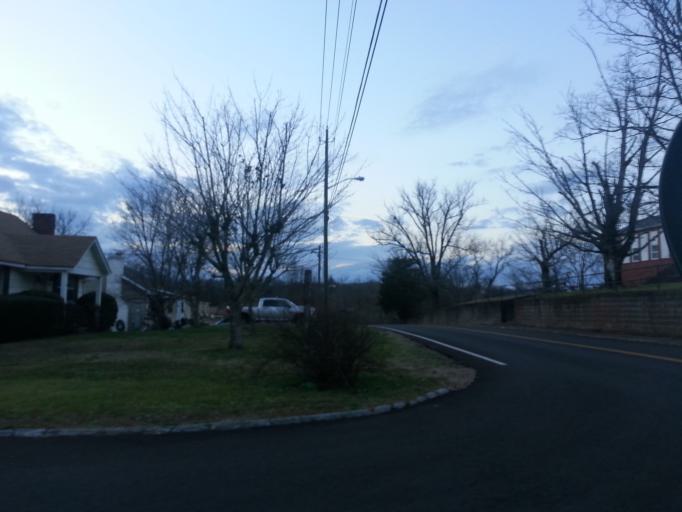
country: US
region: Tennessee
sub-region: Knox County
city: Knoxville
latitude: 35.9388
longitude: -83.8967
